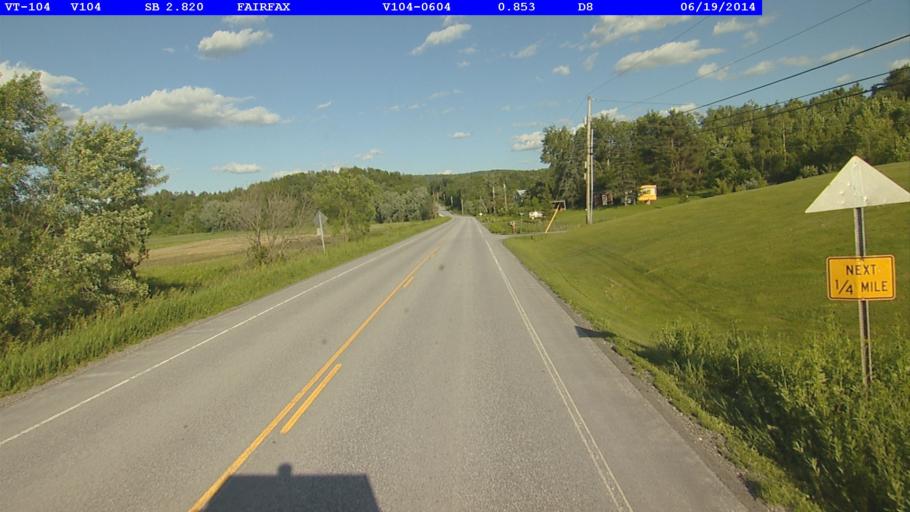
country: US
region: Vermont
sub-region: Chittenden County
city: Jericho
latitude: 44.6420
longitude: -72.9417
